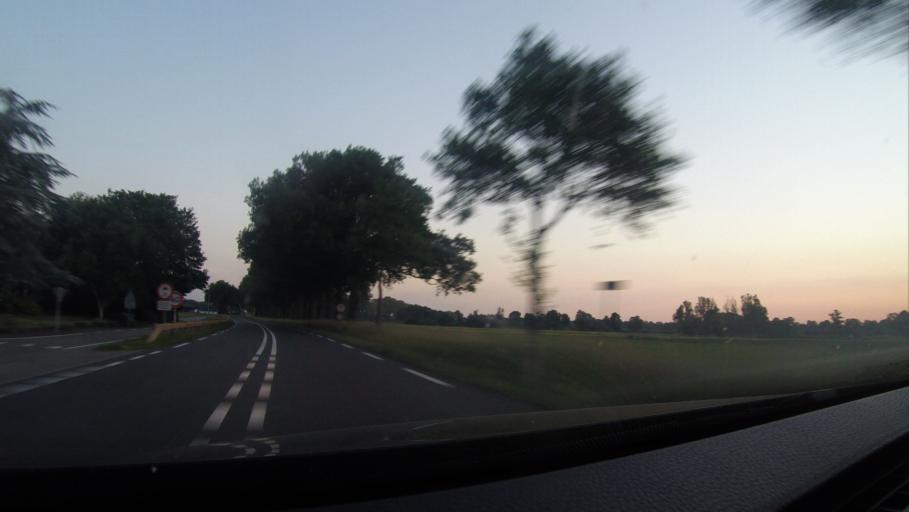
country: NL
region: Gelderland
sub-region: Gemeente Lochem
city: Laren
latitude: 52.1819
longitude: 6.3814
